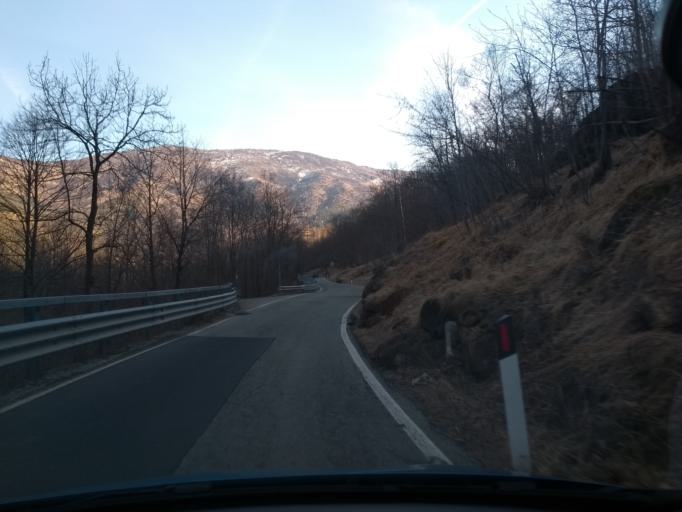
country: IT
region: Piedmont
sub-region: Provincia di Torino
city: La Villa
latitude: 45.2438
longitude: 7.4339
